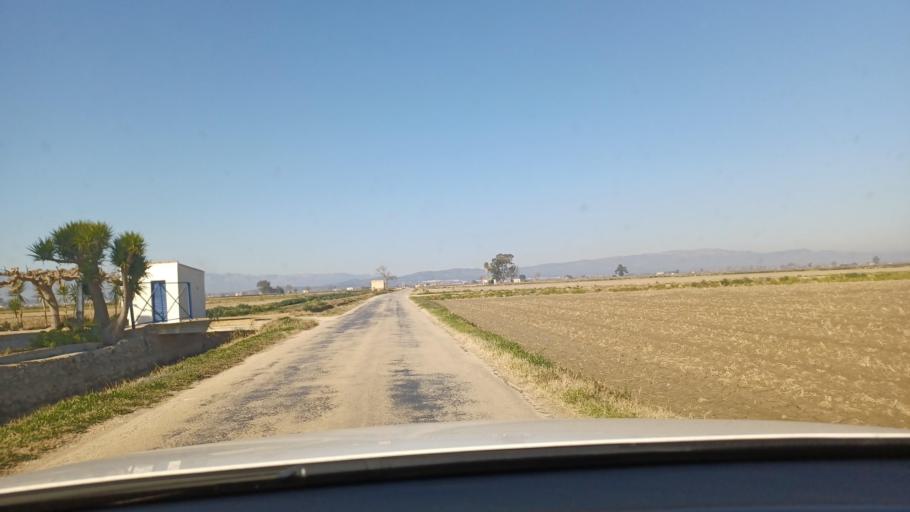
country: ES
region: Catalonia
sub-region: Provincia de Tarragona
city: Deltebre
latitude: 40.6835
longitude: 0.6560
